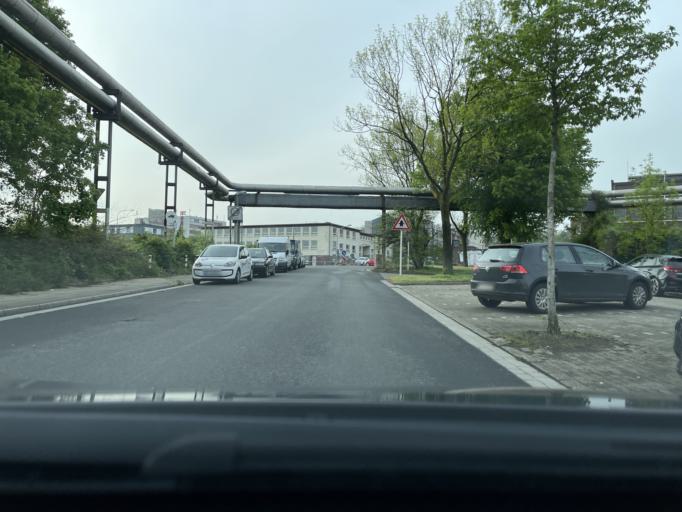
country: DE
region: North Rhine-Westphalia
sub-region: Regierungsbezirk Dusseldorf
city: Essen
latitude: 51.4480
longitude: 6.9898
